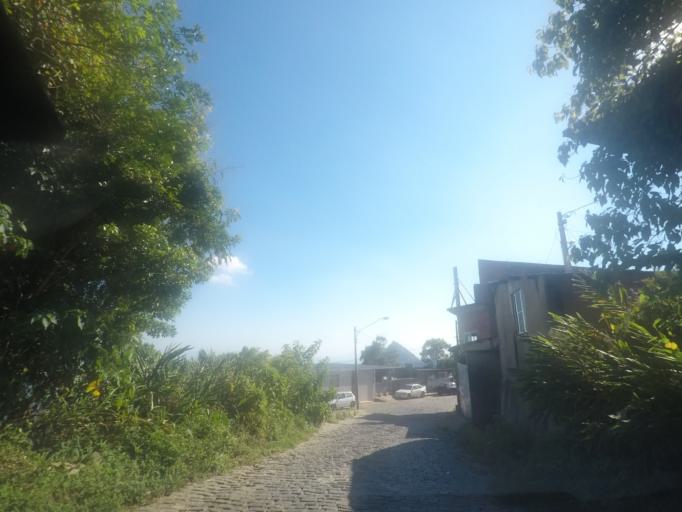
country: BR
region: Rio de Janeiro
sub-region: Petropolis
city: Petropolis
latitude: -22.5460
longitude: -43.1998
